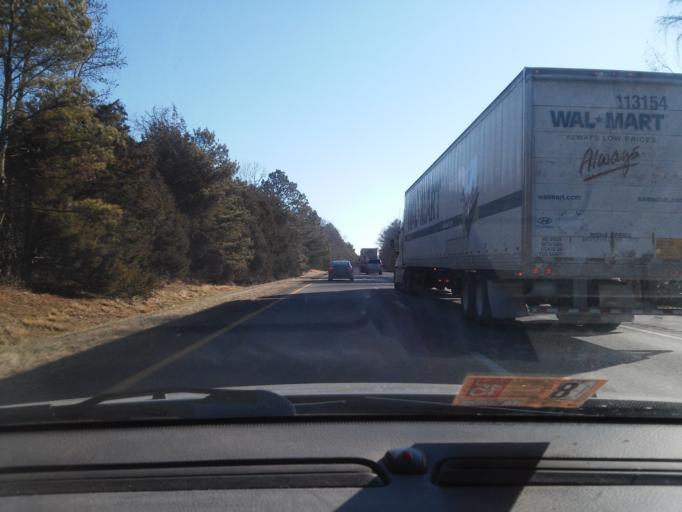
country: US
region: Virginia
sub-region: Henrico County
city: Wyndham
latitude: 37.6955
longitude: -77.7177
